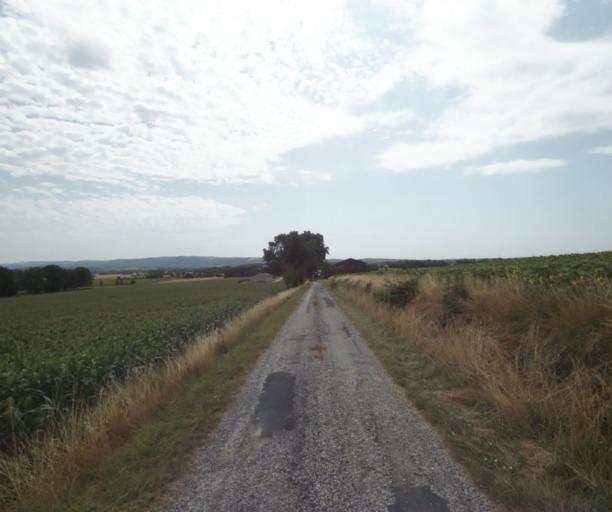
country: FR
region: Midi-Pyrenees
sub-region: Departement de la Haute-Garonne
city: Saint-Felix-Lauragais
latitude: 43.4361
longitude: 1.8987
